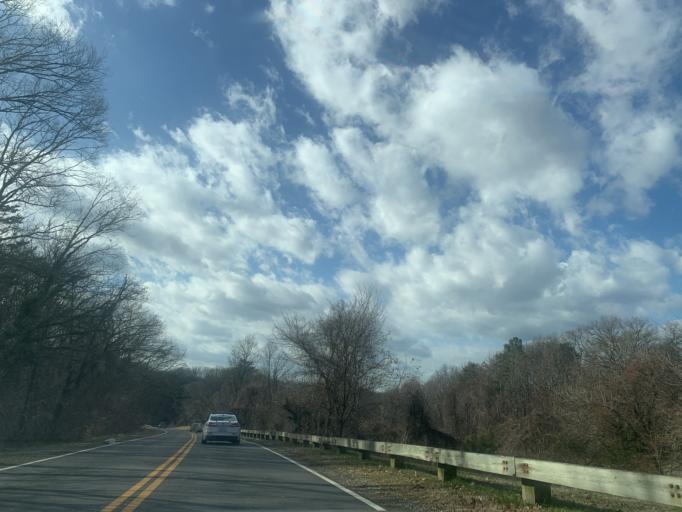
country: US
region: Maryland
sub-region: Prince George's County
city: Coral Hills
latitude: 38.8808
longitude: -76.9460
